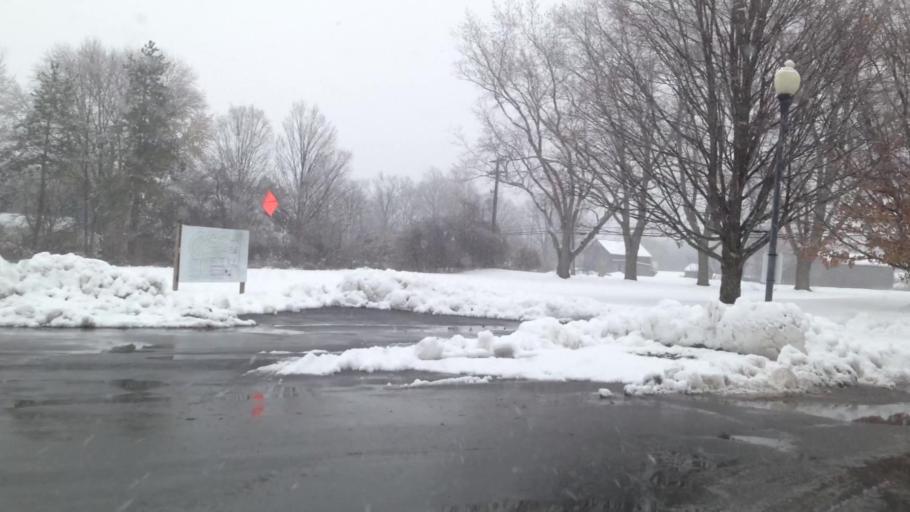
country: US
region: New York
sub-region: Onondaga County
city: Elbridge
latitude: 43.0391
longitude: -76.4151
